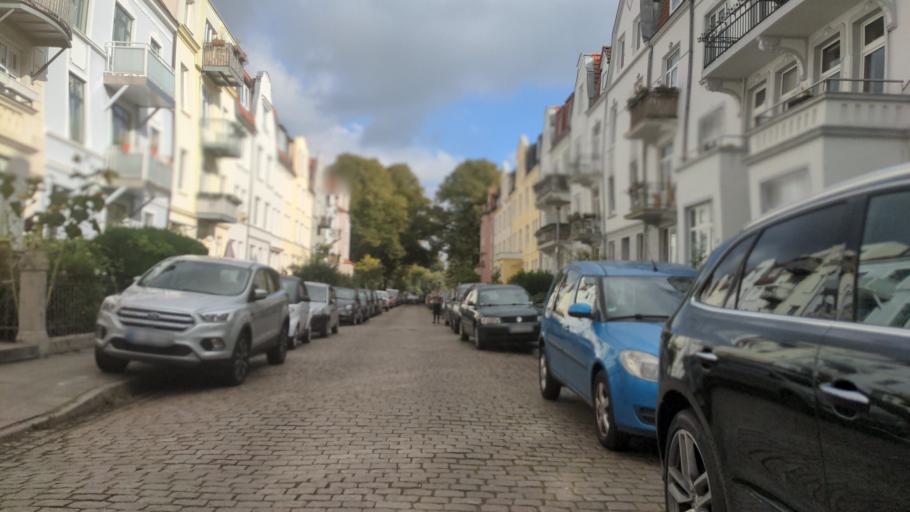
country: DE
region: Schleswig-Holstein
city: Luebeck
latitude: 53.8678
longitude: 10.7019
